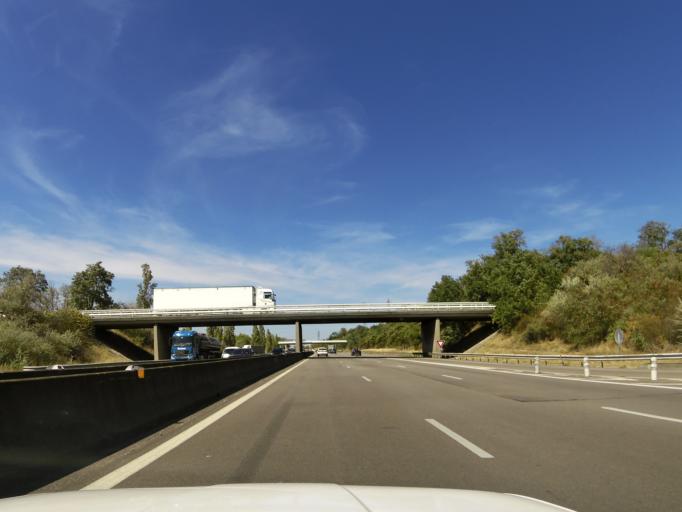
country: FR
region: Rhone-Alpes
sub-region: Departement de l'Isere
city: Chanas
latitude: 45.3232
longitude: 4.8121
